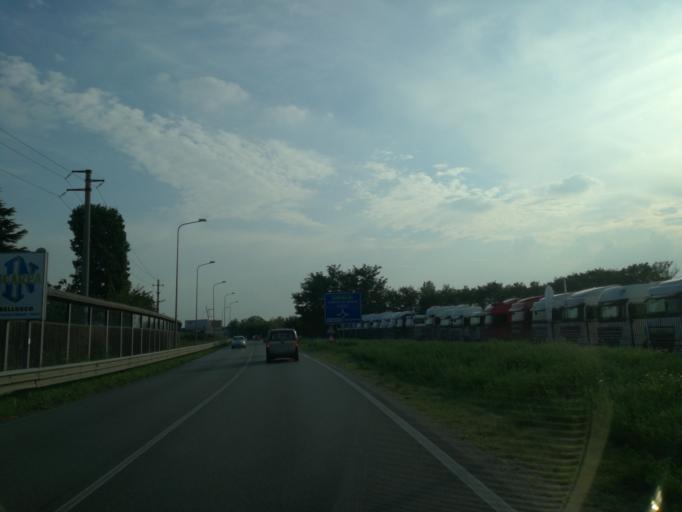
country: IT
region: Lombardy
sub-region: Citta metropolitana di Milano
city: Carugate
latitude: 45.5563
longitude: 9.3337
